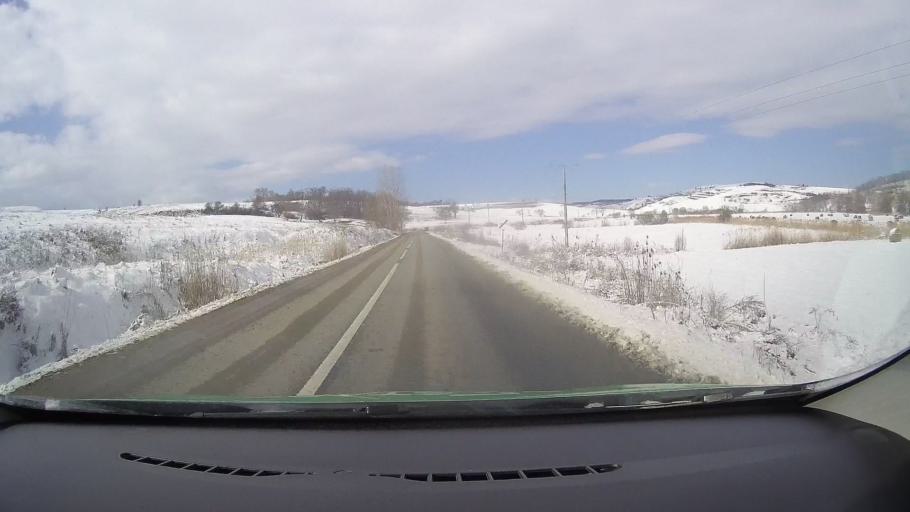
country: RO
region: Sibiu
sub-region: Comuna Altina
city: Altina
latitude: 45.9695
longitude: 24.4692
